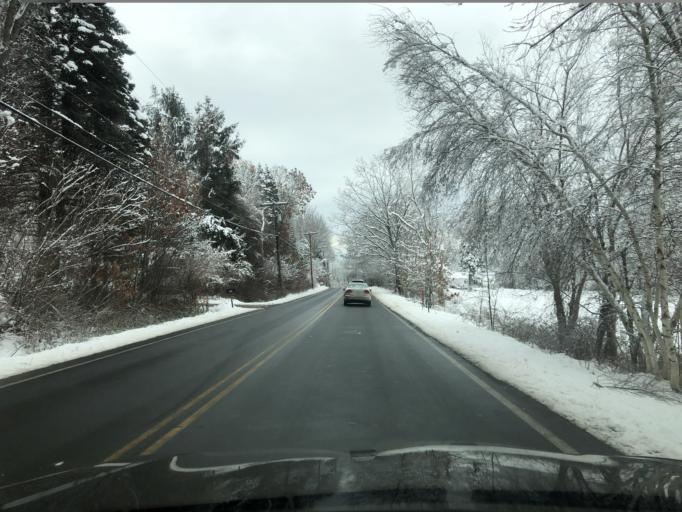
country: US
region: New Hampshire
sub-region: Strafford County
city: Dover
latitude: 43.2209
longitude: -70.8621
